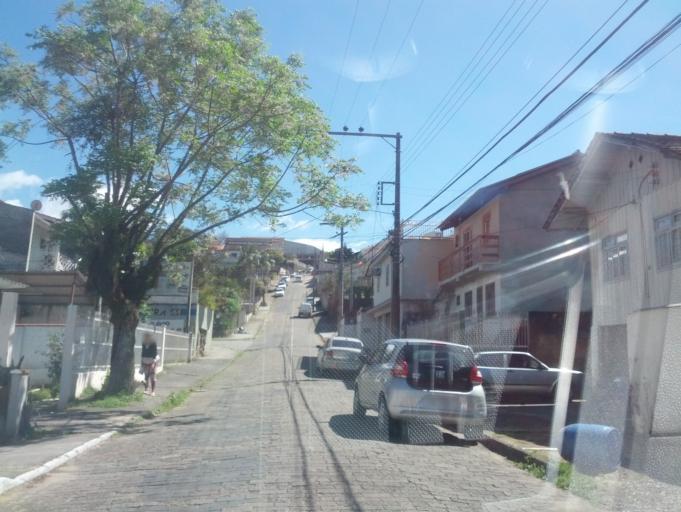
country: BR
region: Santa Catarina
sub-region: Blumenau
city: Blumenau
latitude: -26.9094
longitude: -49.0882
